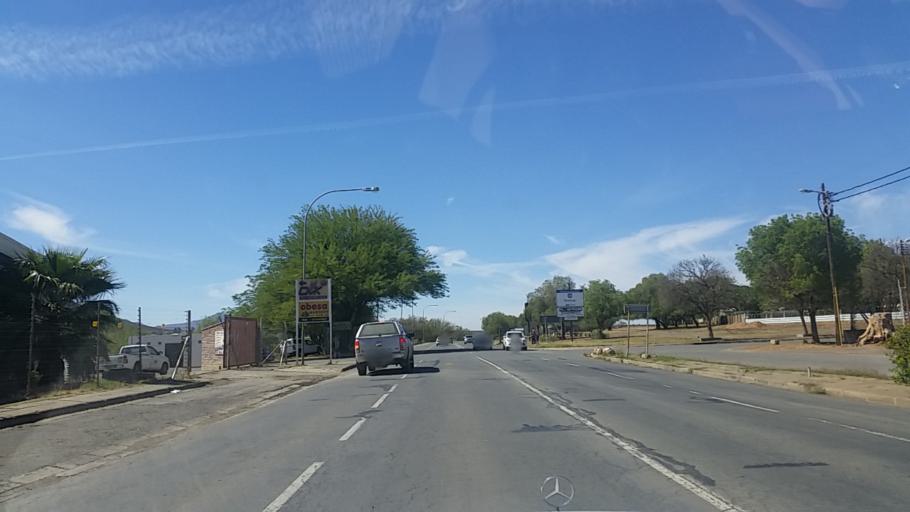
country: ZA
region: Eastern Cape
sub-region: Cacadu District Municipality
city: Graaff-Reinet
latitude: -32.2668
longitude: 24.5433
